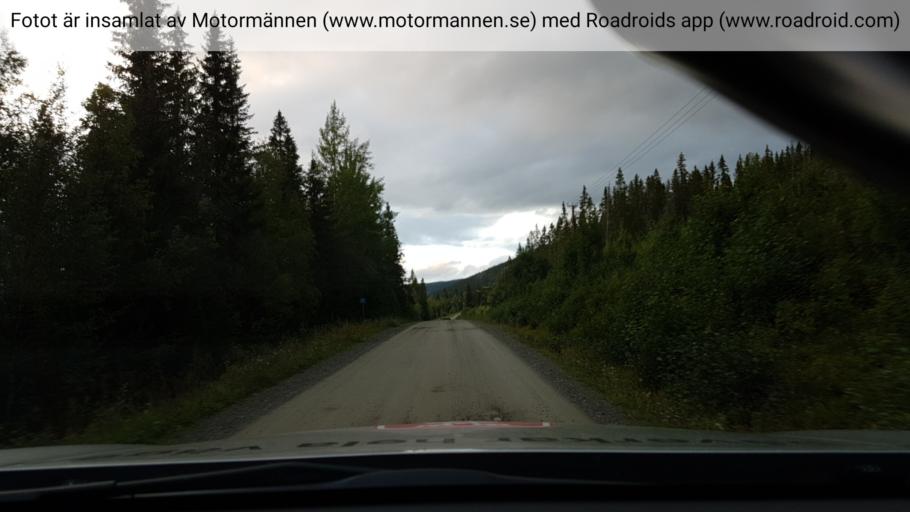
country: SE
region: Vaesterbotten
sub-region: Vilhelmina Kommun
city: Sjoberg
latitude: 65.5990
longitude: 15.2799
